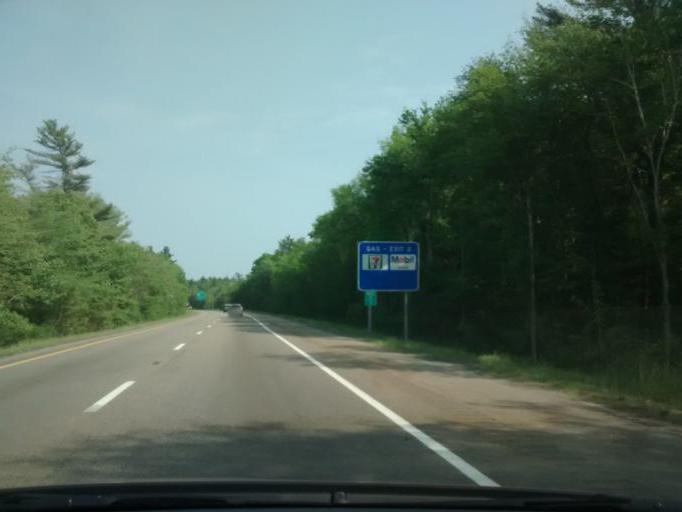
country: US
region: Massachusetts
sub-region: Plymouth County
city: West Wareham
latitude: 41.8171
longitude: -70.7995
